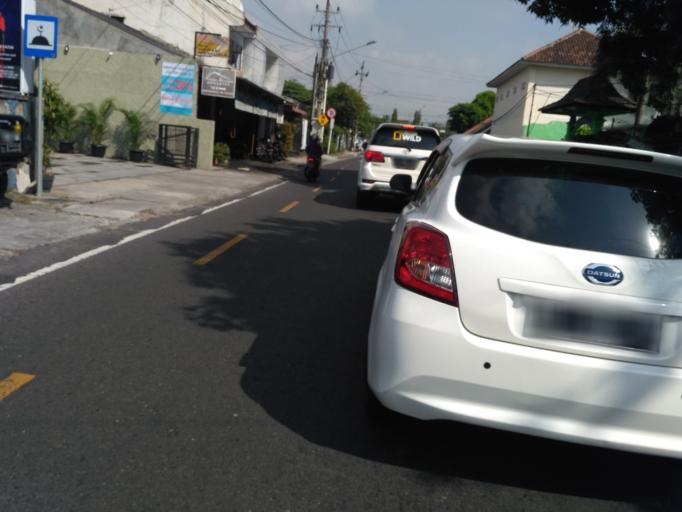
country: ID
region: Daerah Istimewa Yogyakarta
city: Yogyakarta
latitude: -7.7782
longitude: 110.3685
